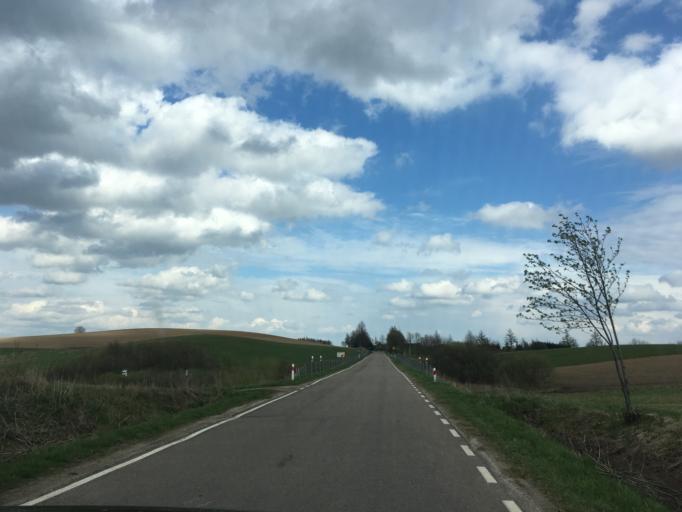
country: LT
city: Virbalis
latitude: 54.3647
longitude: 22.8384
